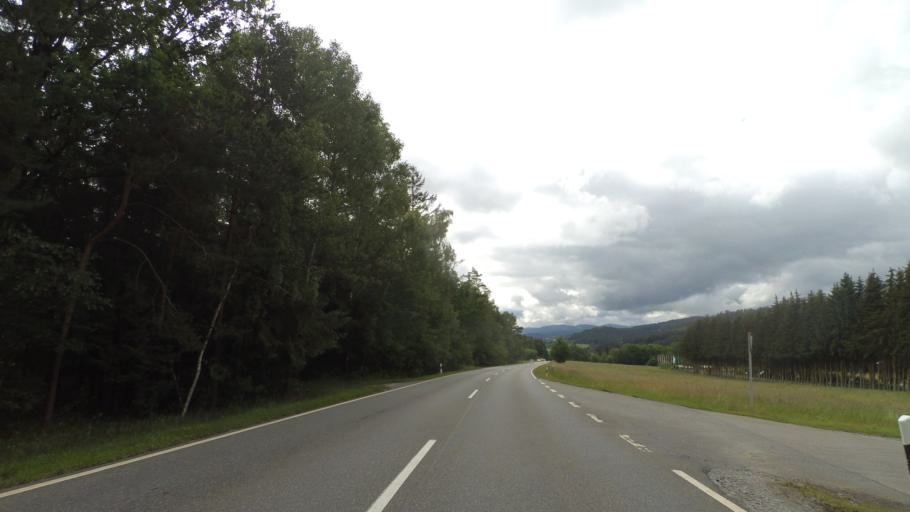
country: DE
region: Bavaria
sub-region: Lower Bavaria
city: Prackenbach
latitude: 49.0867
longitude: 12.8526
